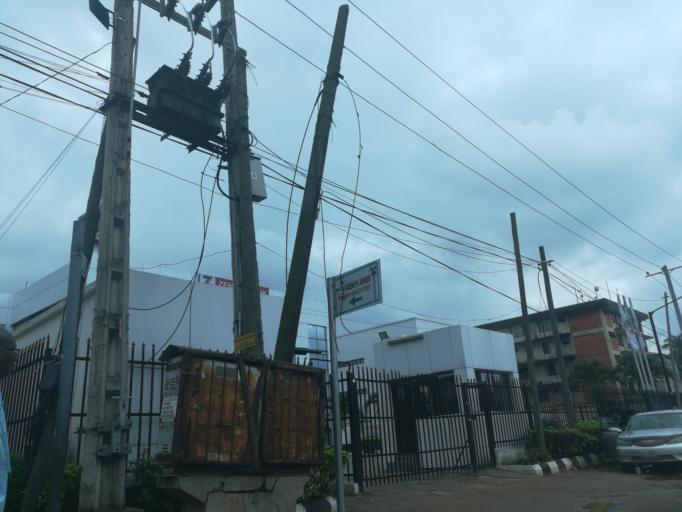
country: NG
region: Lagos
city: Ikeja
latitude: 6.6133
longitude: 3.3459
